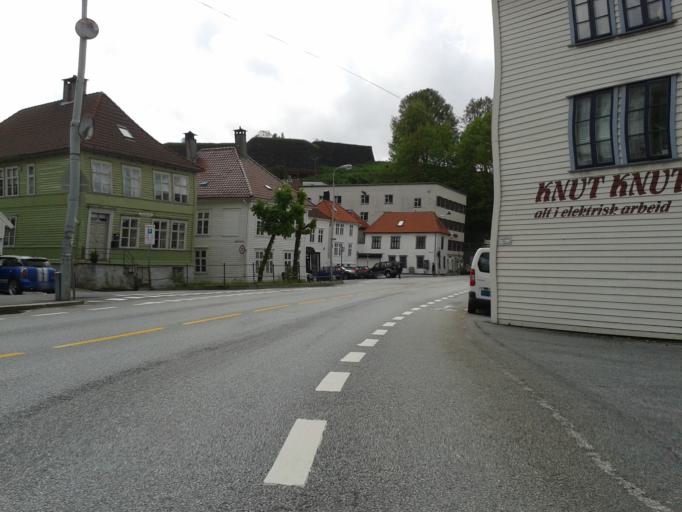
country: NO
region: Hordaland
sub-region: Bergen
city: Bergen
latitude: 60.4030
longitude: 5.3213
